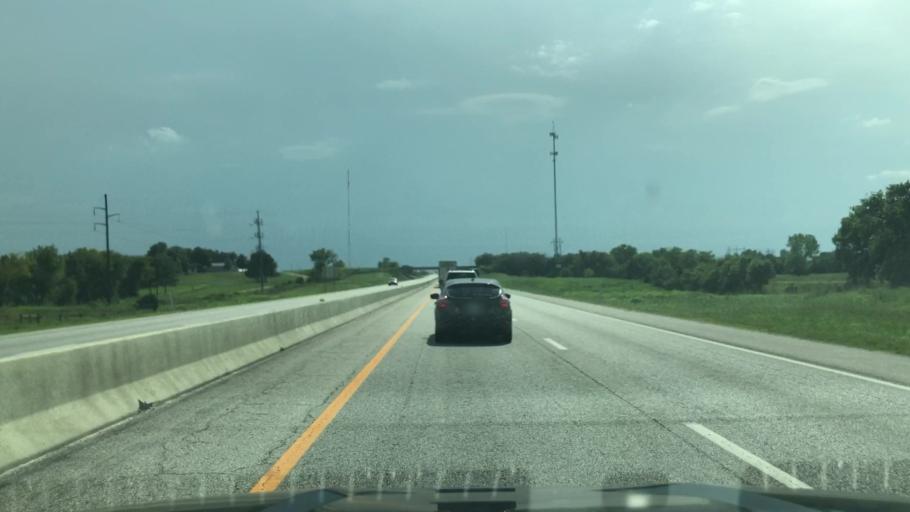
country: US
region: Oklahoma
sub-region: Craig County
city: Vinita
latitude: 36.6414
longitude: -95.1214
